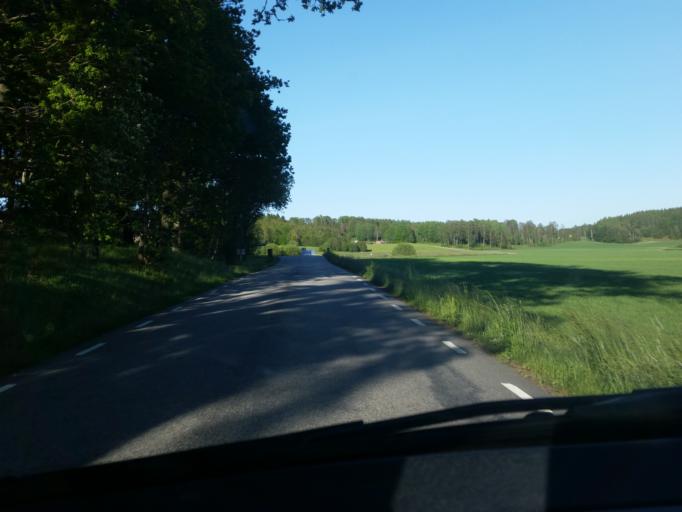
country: SE
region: Vaestra Goetaland
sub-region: Fargelanda Kommun
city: Faergelanda
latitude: 58.5160
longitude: 11.9671
